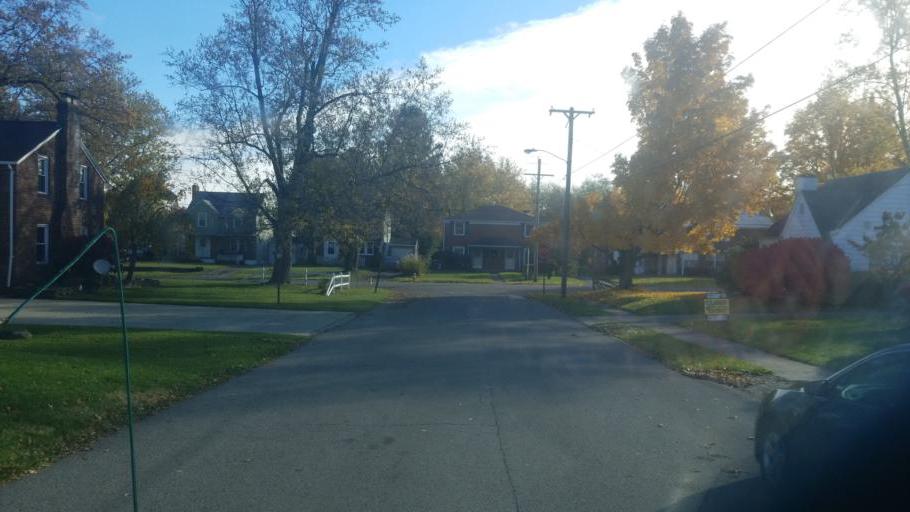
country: US
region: Ohio
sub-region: Richland County
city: Mansfield
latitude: 40.7483
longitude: -82.5333
